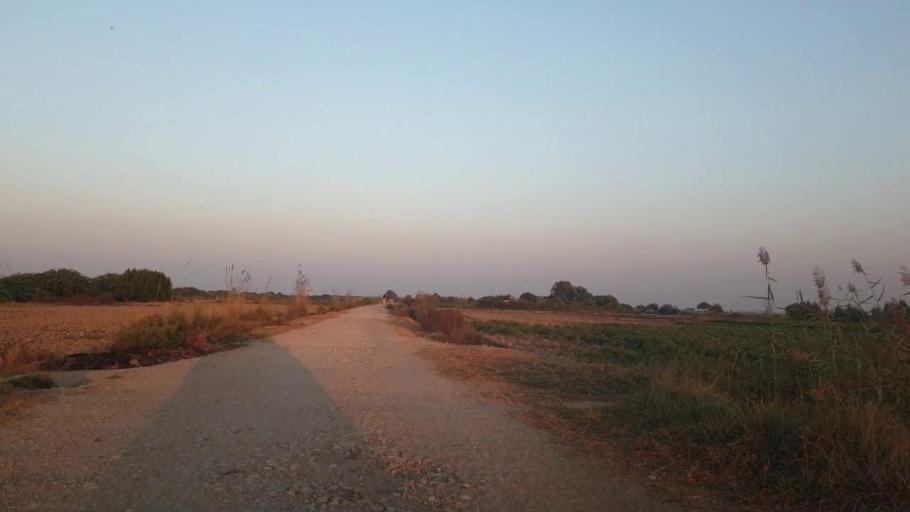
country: PK
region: Sindh
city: Mirpur Sakro
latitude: 24.4206
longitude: 67.5836
